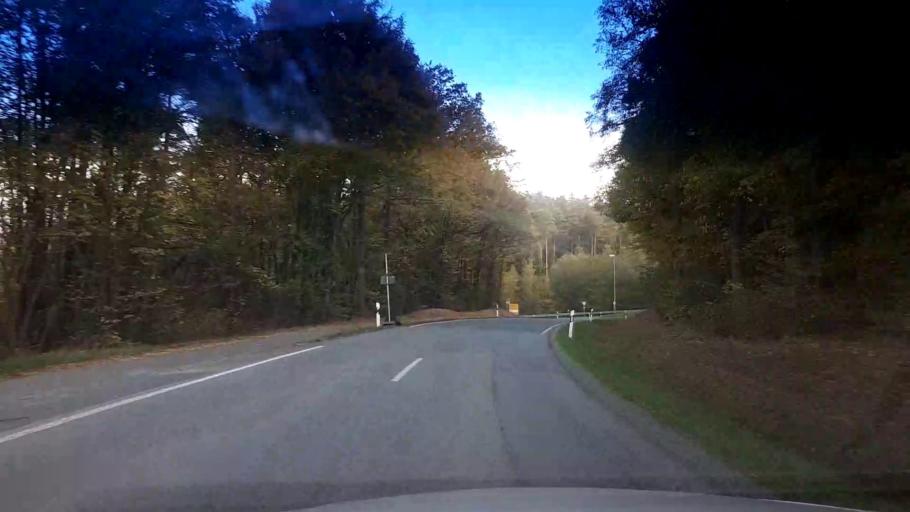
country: DE
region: Bavaria
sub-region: Upper Franconia
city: Weismain
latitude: 50.0912
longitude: 11.2479
